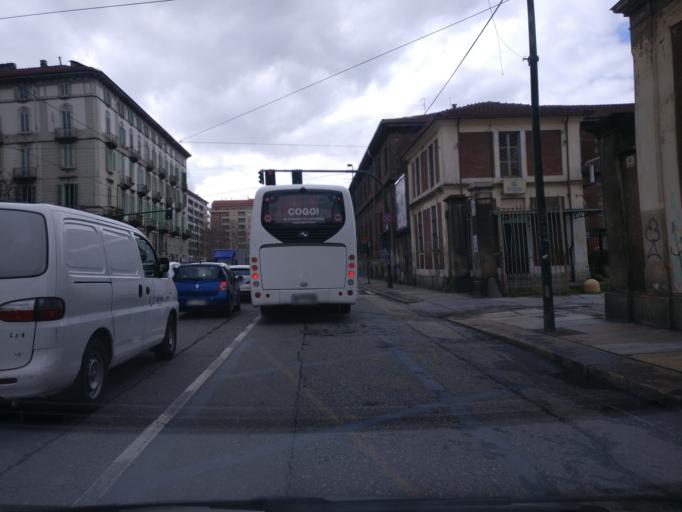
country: IT
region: Piedmont
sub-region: Provincia di Torino
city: Turin
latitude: 45.0530
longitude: 7.6751
